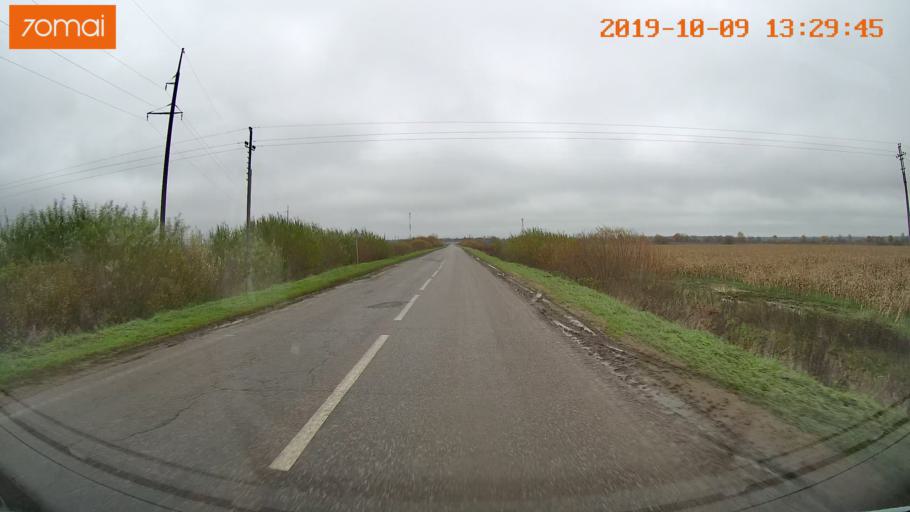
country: RU
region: Jaroslavl
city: Lyubim
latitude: 58.3182
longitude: 40.9950
